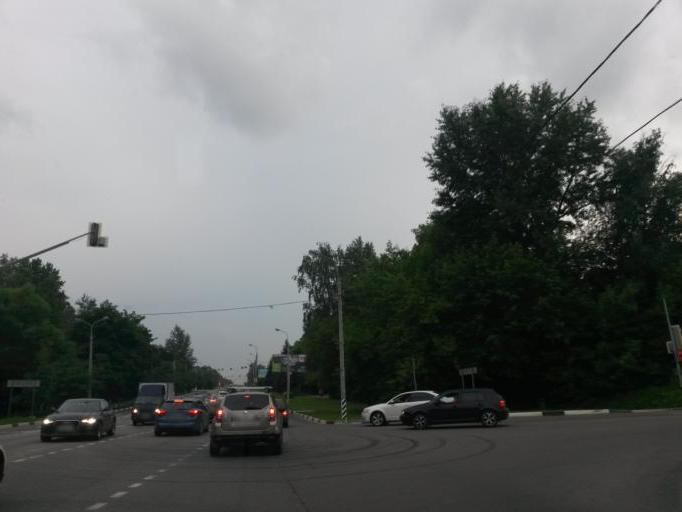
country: RU
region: Moskovskaya
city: Domodedovo
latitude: 55.4245
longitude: 37.7734
